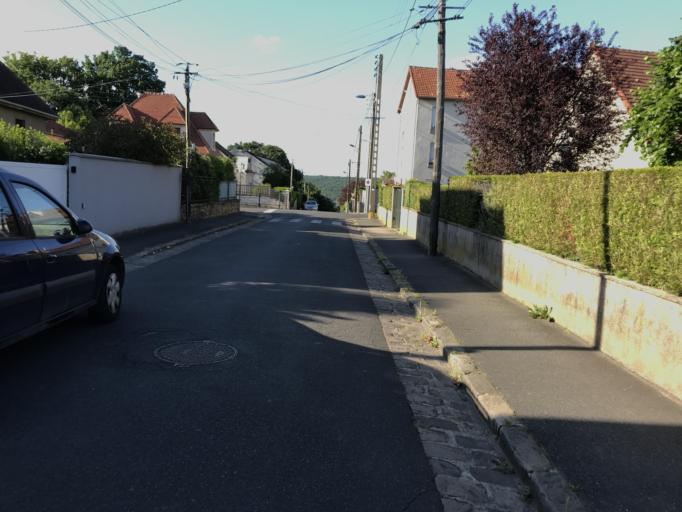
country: FR
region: Ile-de-France
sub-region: Departement de l'Essonne
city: Igny
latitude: 48.7252
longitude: 2.2301
